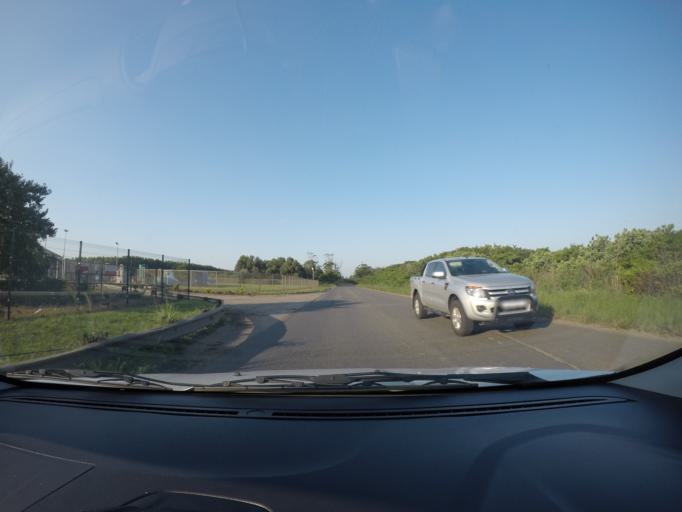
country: ZA
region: KwaZulu-Natal
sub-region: uThungulu District Municipality
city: Richards Bay
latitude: -28.7585
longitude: 32.0032
